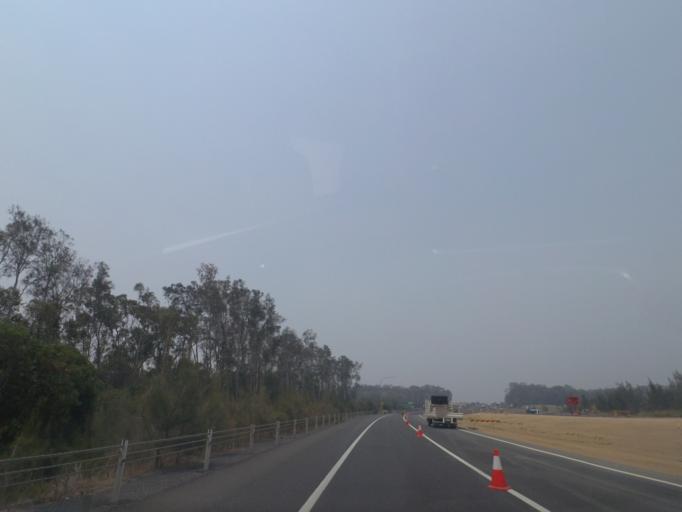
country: AU
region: New South Wales
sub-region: Ballina
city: Ballina
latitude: -28.8676
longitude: 153.4938
